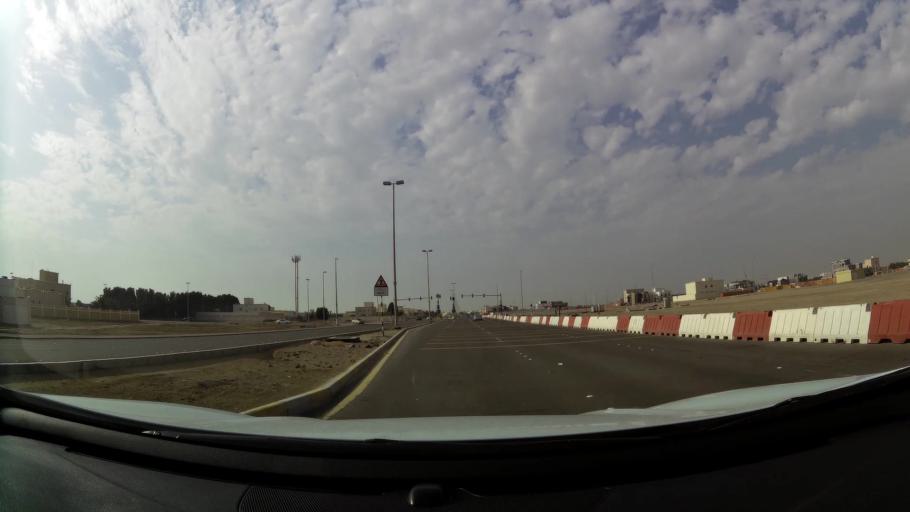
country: AE
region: Abu Dhabi
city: Abu Dhabi
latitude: 24.3379
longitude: 54.5708
